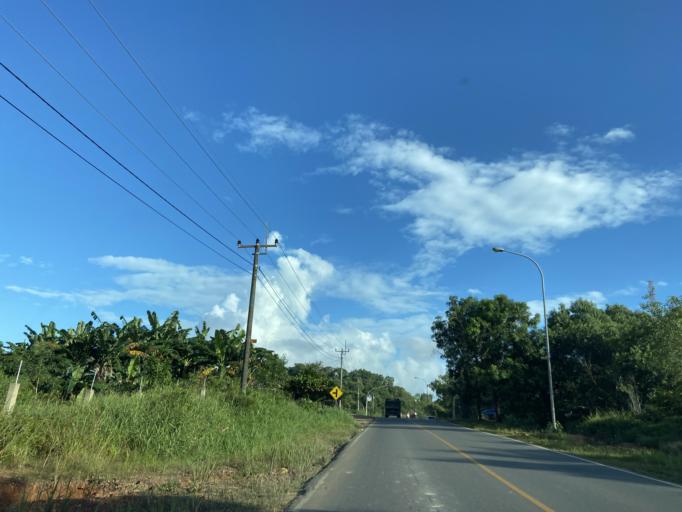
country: SG
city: Singapore
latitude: 1.0030
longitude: 104.0259
